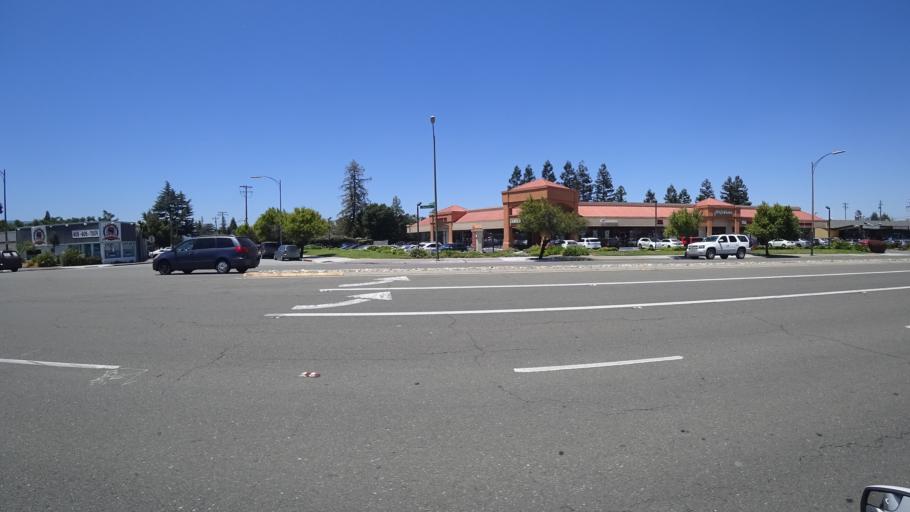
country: US
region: California
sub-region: Santa Clara County
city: Cambrian Park
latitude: 37.2651
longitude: -121.9419
